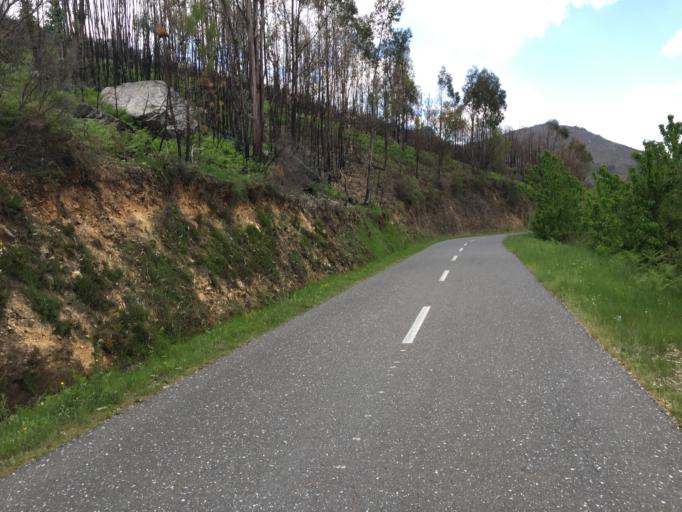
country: PT
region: Coimbra
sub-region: Pampilhosa da Serra
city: Pampilhosa da Serra
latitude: 40.0982
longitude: -7.8635
